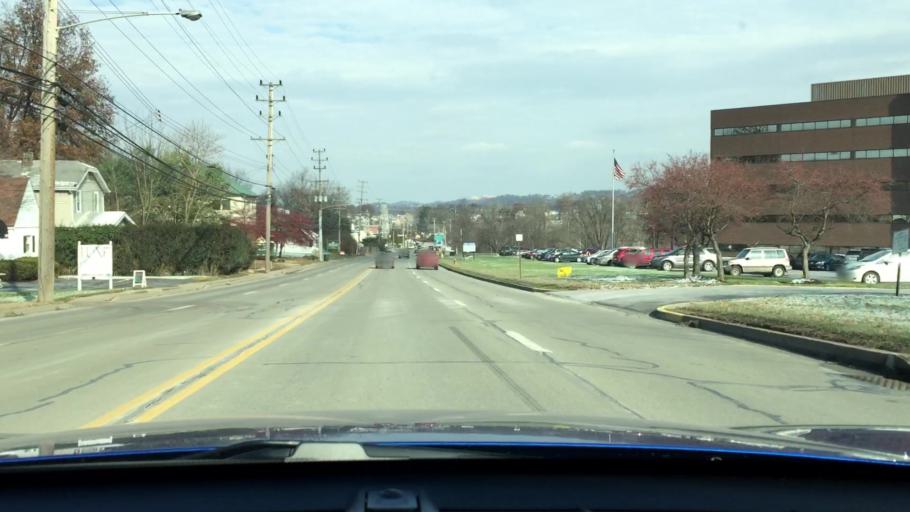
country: US
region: Pennsylvania
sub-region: Allegheny County
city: Heidelberg
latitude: 40.3782
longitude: -80.0967
